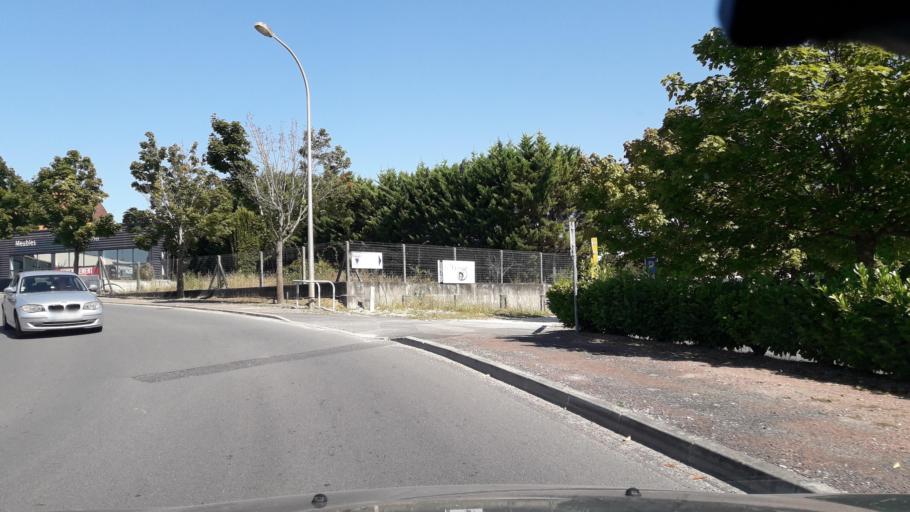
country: FR
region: Poitou-Charentes
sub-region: Departement de la Charente
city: Gond-Pontouvre
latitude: 45.6922
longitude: 0.1869
